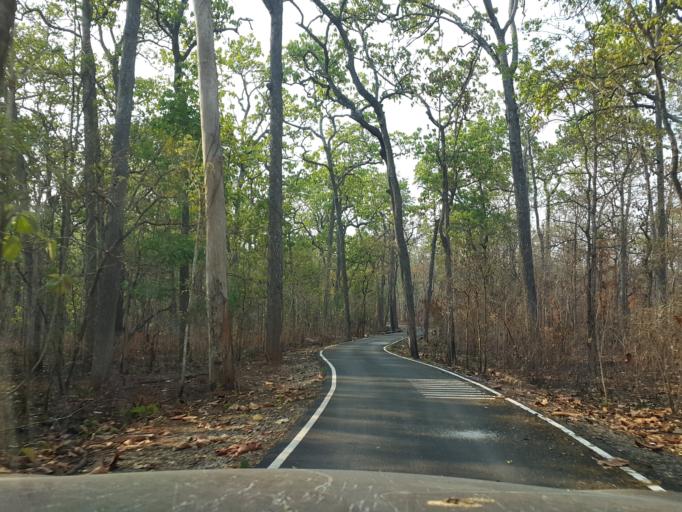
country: TH
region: Lamphun
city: Li
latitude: 17.6152
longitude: 98.8732
